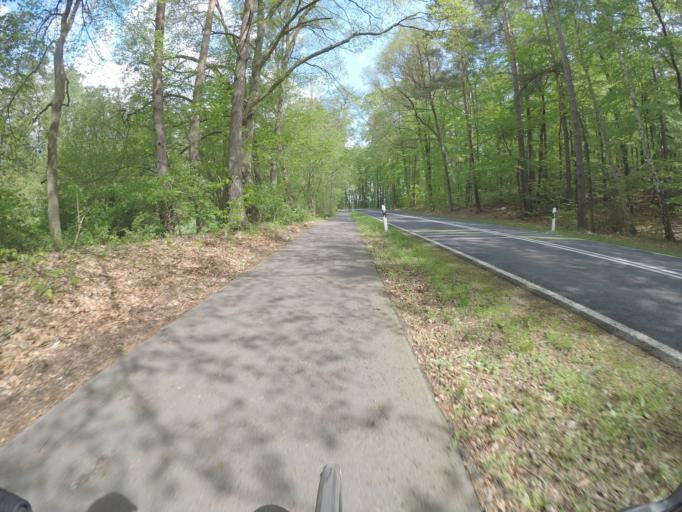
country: DE
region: Brandenburg
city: Joachimsthal
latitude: 52.9274
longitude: 13.7049
